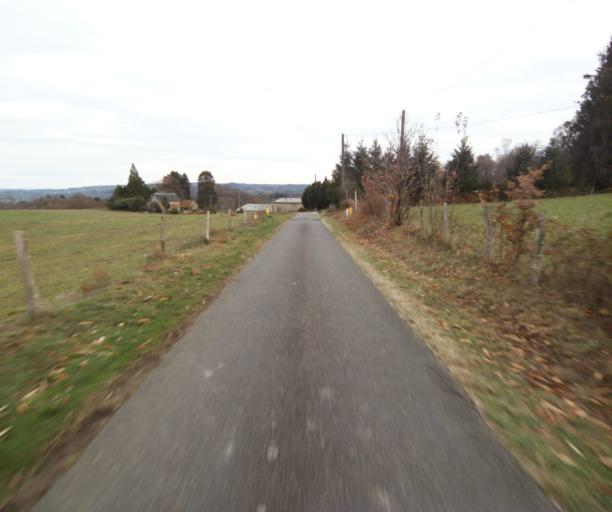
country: FR
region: Limousin
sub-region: Departement de la Correze
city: Chameyrat
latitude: 45.2342
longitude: 1.6625
